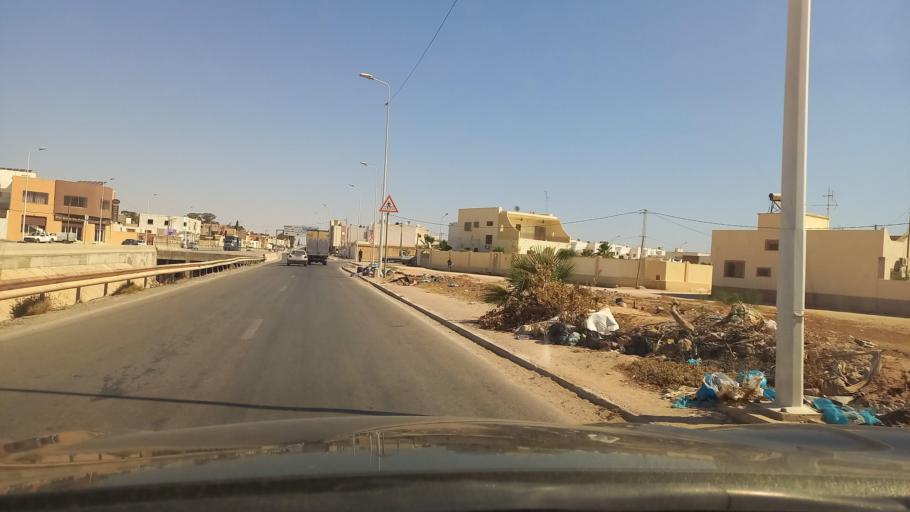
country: TN
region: Safaqis
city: Sfax
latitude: 34.7285
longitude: 10.7259
